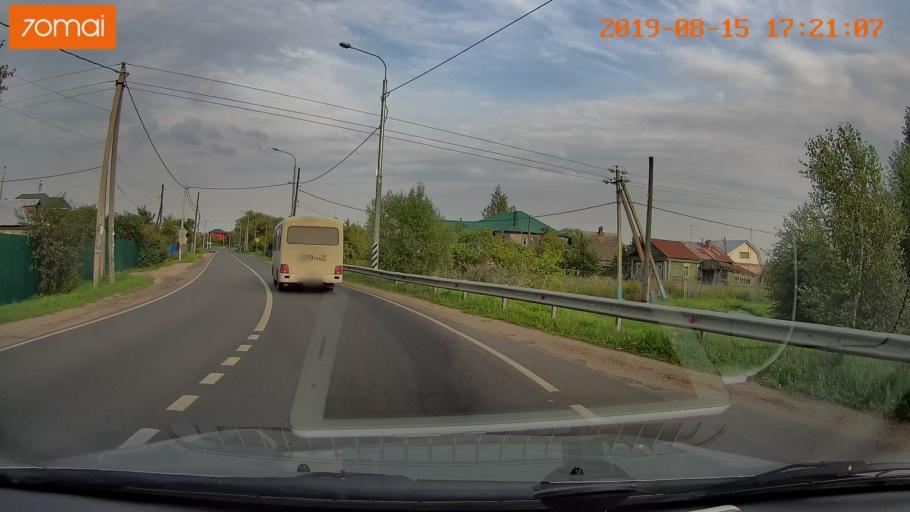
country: RU
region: Moskovskaya
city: Ashitkovo
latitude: 55.4215
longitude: 38.5643
